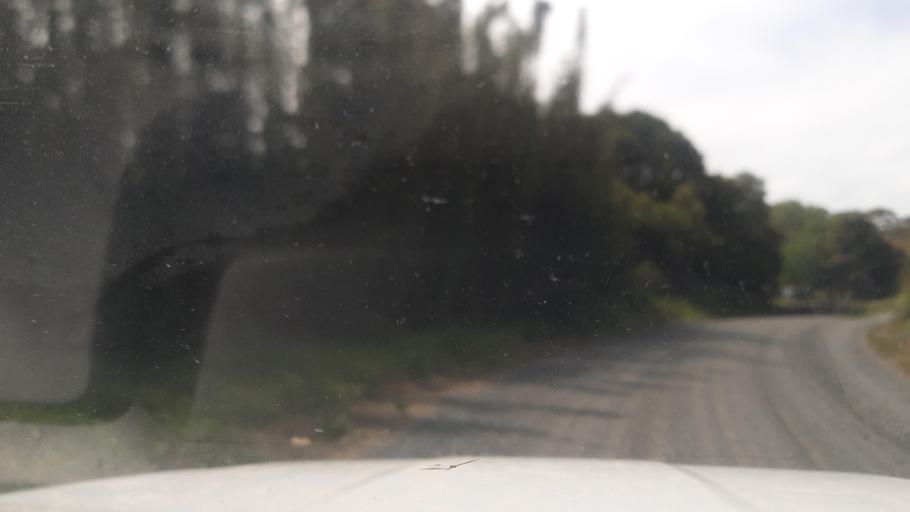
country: NZ
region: Northland
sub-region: Far North District
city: Kaitaia
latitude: -34.8363
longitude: 173.1240
